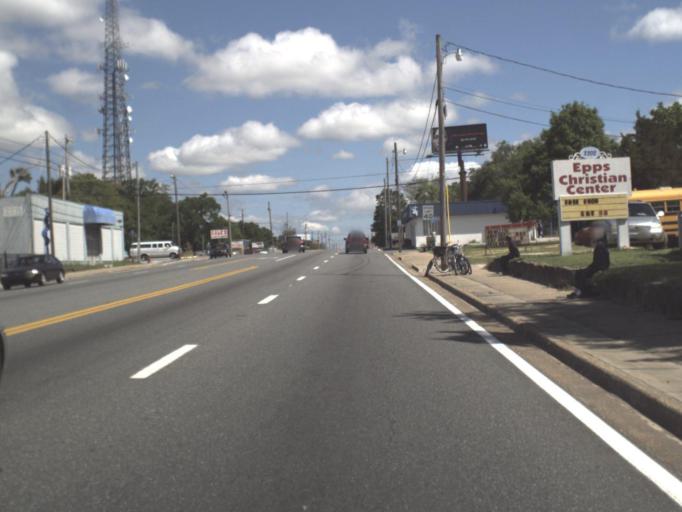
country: US
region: Florida
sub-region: Escambia County
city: Goulding
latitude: 30.4352
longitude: -87.2403
